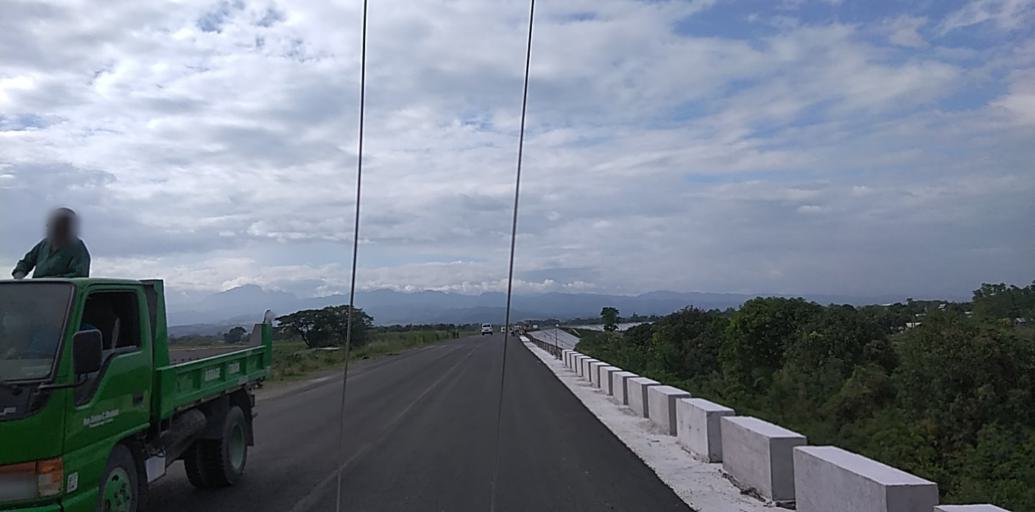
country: PH
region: Central Luzon
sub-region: Province of Pampanga
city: Pulung Santol
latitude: 15.0603
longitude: 120.5651
